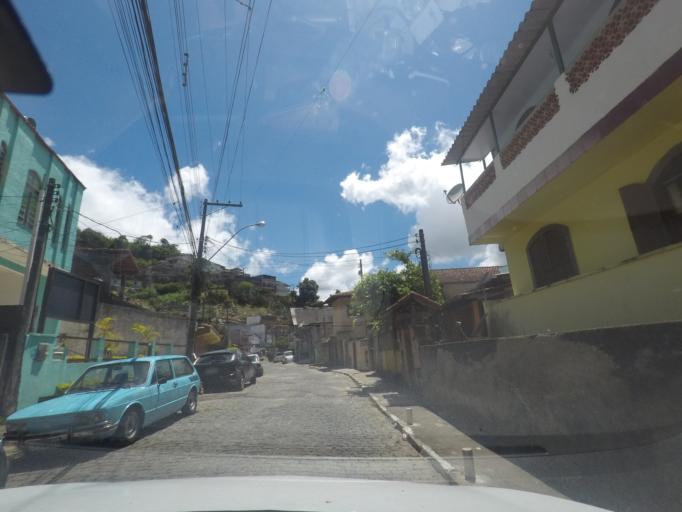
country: BR
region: Rio de Janeiro
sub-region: Teresopolis
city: Teresopolis
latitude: -22.4219
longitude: -42.9864
